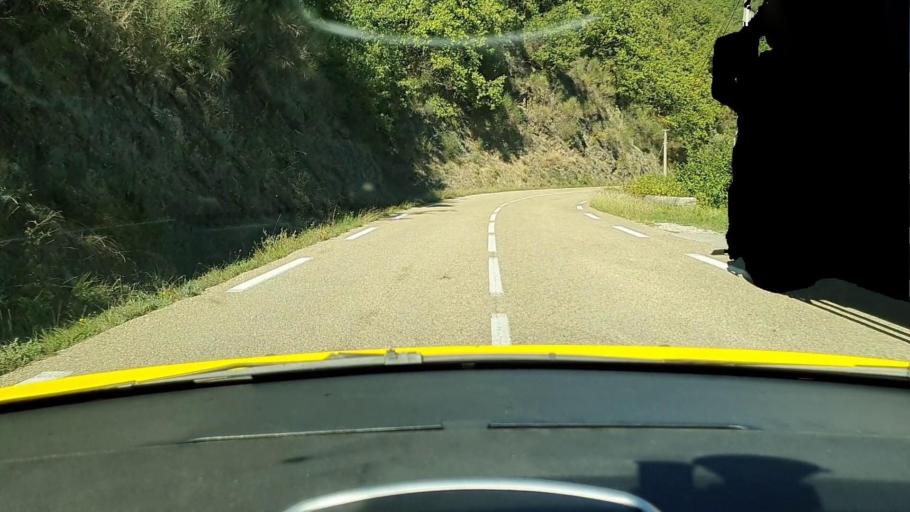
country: FR
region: Languedoc-Roussillon
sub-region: Departement du Gard
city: Le Vigan
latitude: 43.9778
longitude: 3.4672
